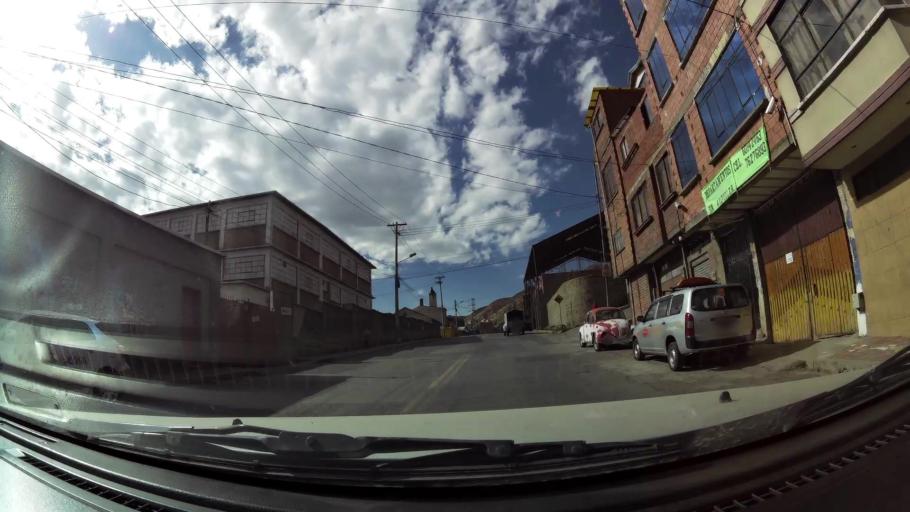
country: BO
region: La Paz
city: La Paz
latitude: -16.4674
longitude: -68.1518
